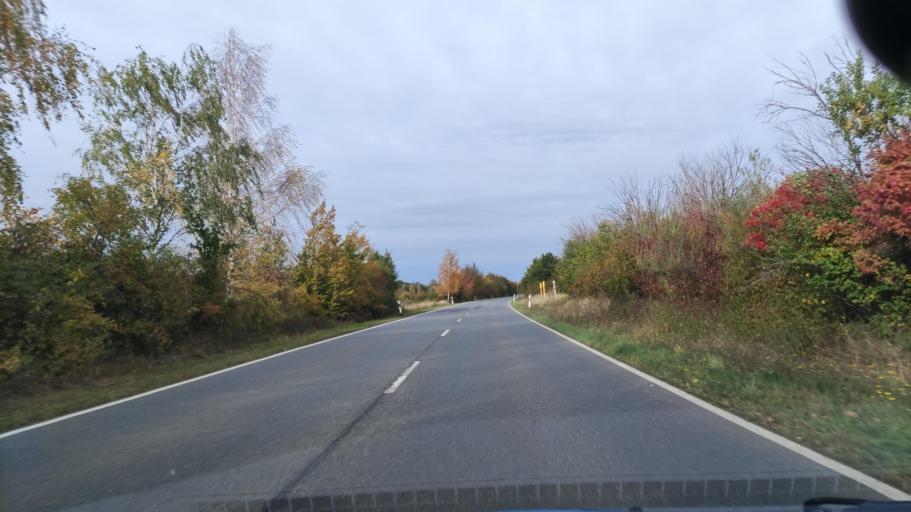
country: DE
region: Saxony-Anhalt
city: Darlingerode
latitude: 51.8640
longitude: 10.7555
